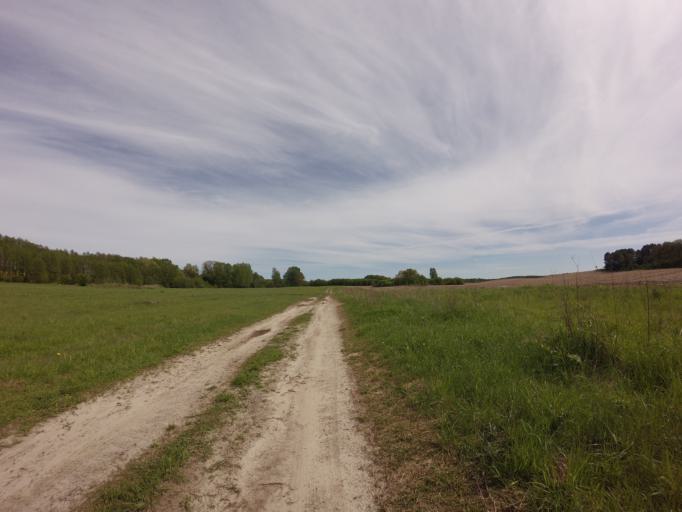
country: PL
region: West Pomeranian Voivodeship
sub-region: Powiat choszczenski
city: Recz
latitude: 53.1604
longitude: 15.5699
